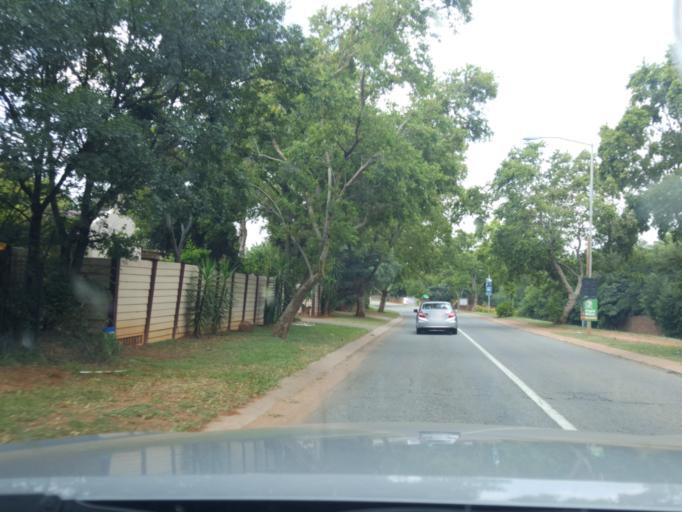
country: ZA
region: Gauteng
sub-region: City of Tshwane Metropolitan Municipality
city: Centurion
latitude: -25.8447
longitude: 28.2681
